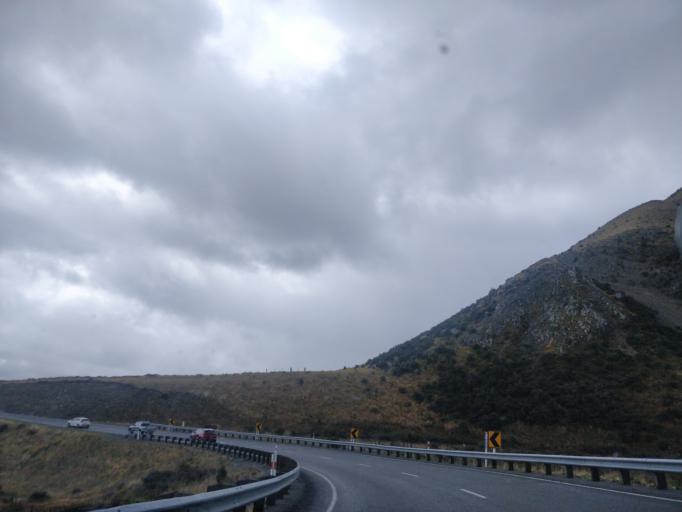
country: NZ
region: Canterbury
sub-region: Ashburton District
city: Methven
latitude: -43.2581
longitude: 171.7139
